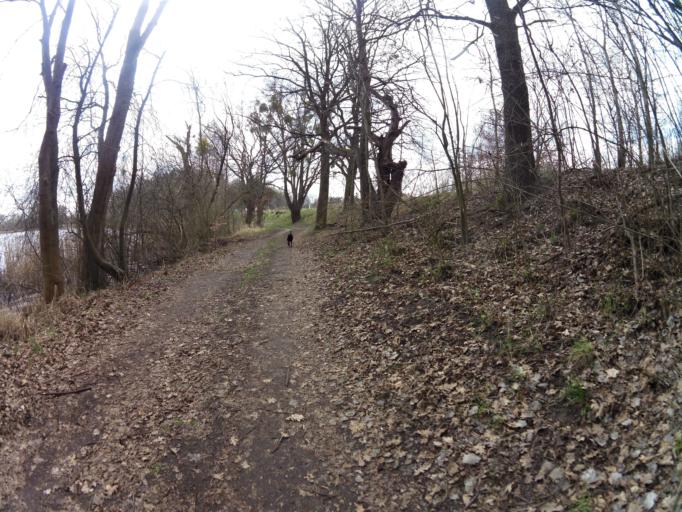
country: PL
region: West Pomeranian Voivodeship
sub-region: Powiat mysliborski
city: Mysliborz
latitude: 52.9373
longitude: 14.8545
